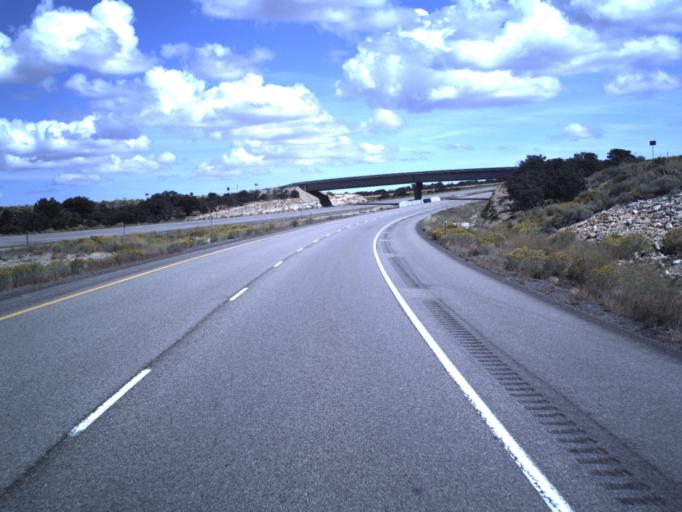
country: US
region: Utah
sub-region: Emery County
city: Ferron
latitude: 38.8558
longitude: -110.9171
